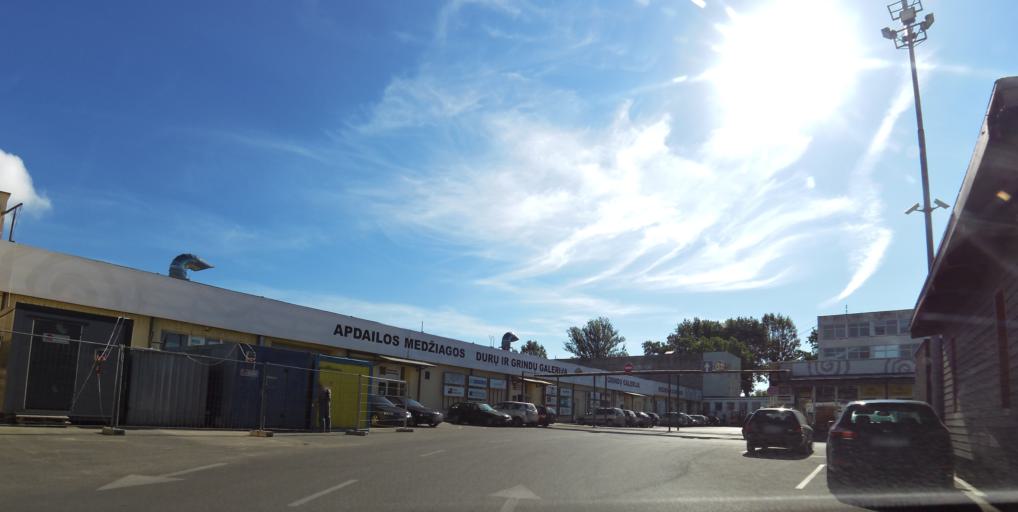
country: LT
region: Vilnius County
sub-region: Vilnius
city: Vilnius
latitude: 54.7153
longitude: 25.2922
